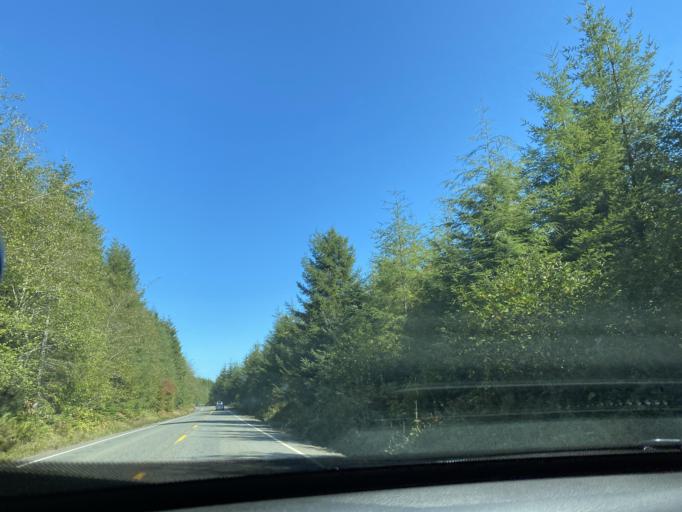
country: US
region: Washington
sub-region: Clallam County
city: Forks
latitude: 47.9319
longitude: -124.4797
